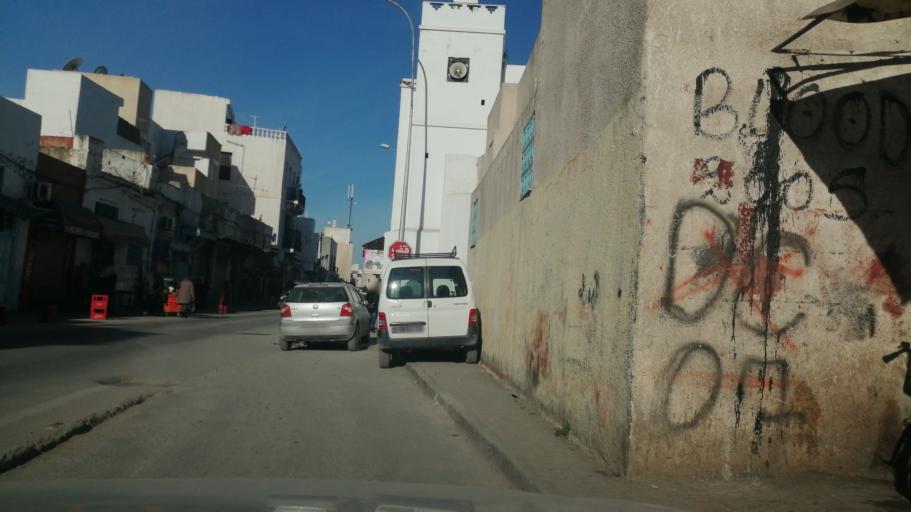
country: TN
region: Tunis
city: Tunis
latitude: 36.8058
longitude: 10.1663
